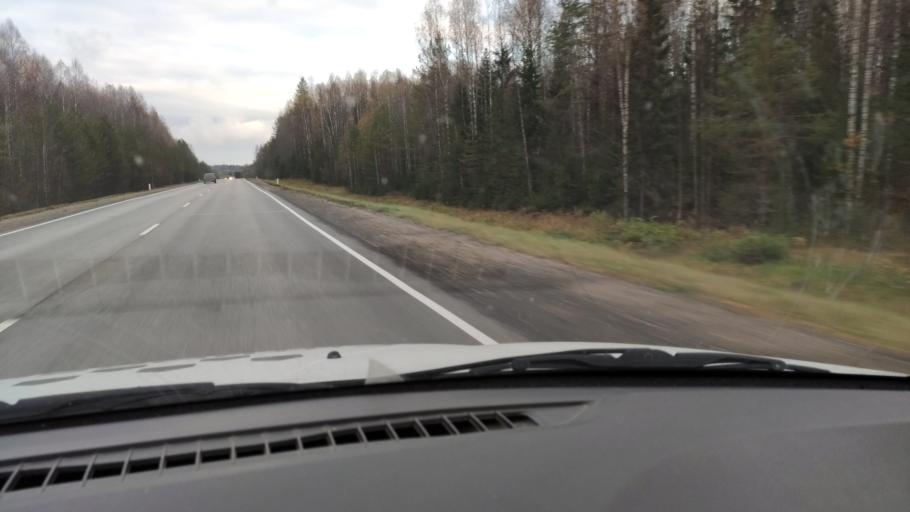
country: RU
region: Kirov
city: Chernaya Kholunitsa
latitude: 58.8283
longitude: 51.7720
